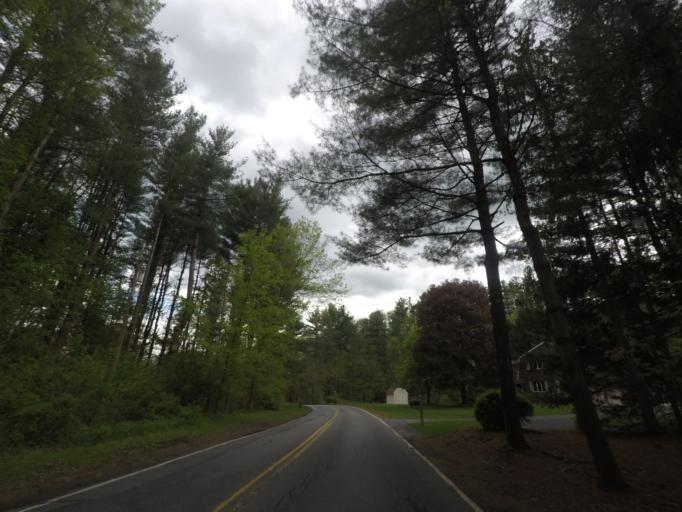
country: US
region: New York
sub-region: Albany County
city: Voorheesville
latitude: 42.6951
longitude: -73.9168
